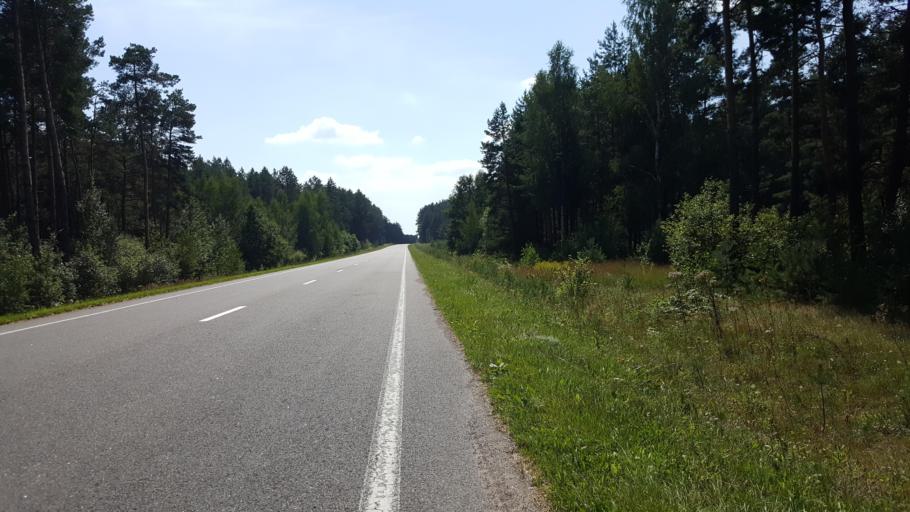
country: PL
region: Podlasie
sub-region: Powiat hajnowski
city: Czeremcha
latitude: 52.5261
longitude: 23.5354
